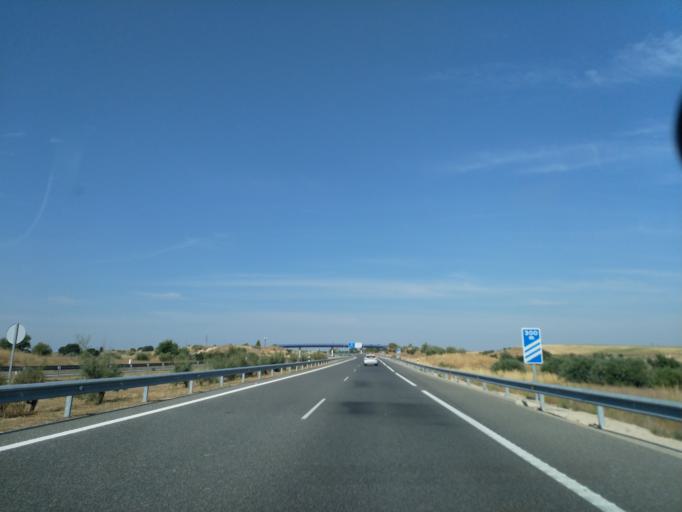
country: ES
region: Madrid
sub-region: Provincia de Madrid
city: Navalcarnero
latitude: 40.2634
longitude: -3.9965
